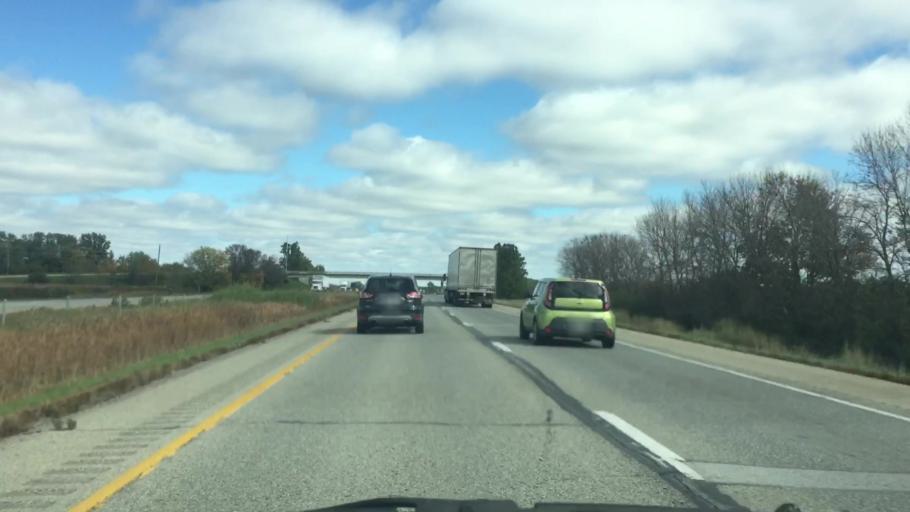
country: US
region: Iowa
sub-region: Jasper County
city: Newton
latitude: 41.6858
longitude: -92.8851
